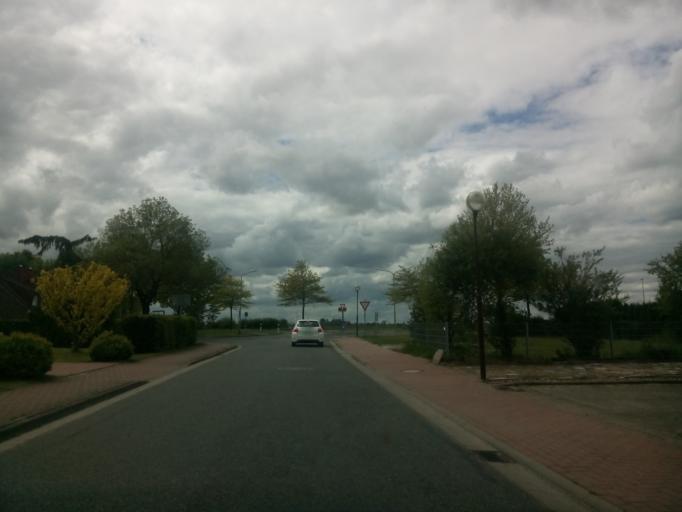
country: DE
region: Lower Saxony
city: Lemwerder
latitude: 53.1507
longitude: 8.6090
